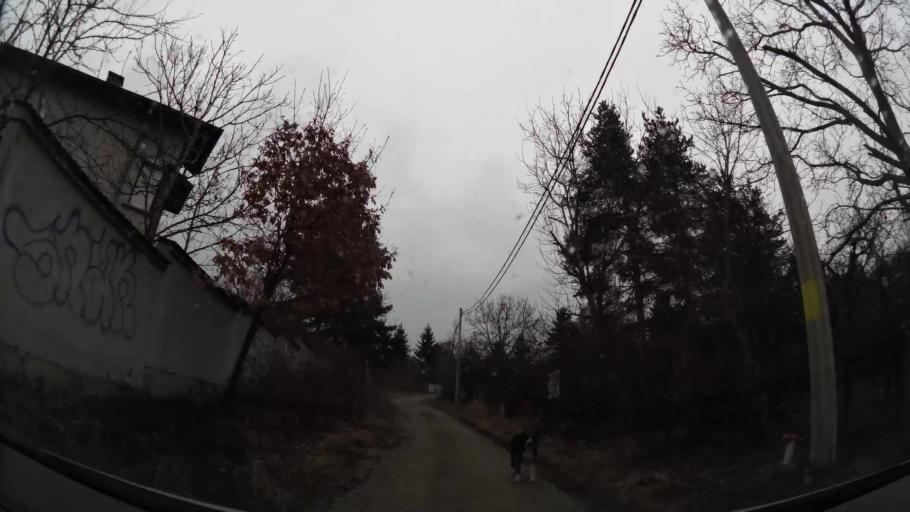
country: BG
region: Sofia-Capital
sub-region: Stolichna Obshtina
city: Sofia
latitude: 42.6006
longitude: 23.3935
